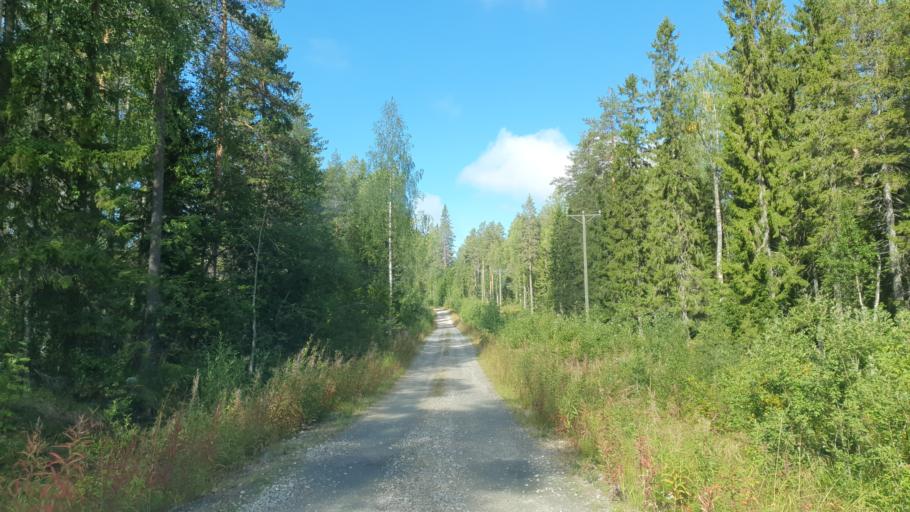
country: FI
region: Kainuu
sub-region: Kehys-Kainuu
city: Kuhmo
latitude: 64.0391
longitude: 29.1387
